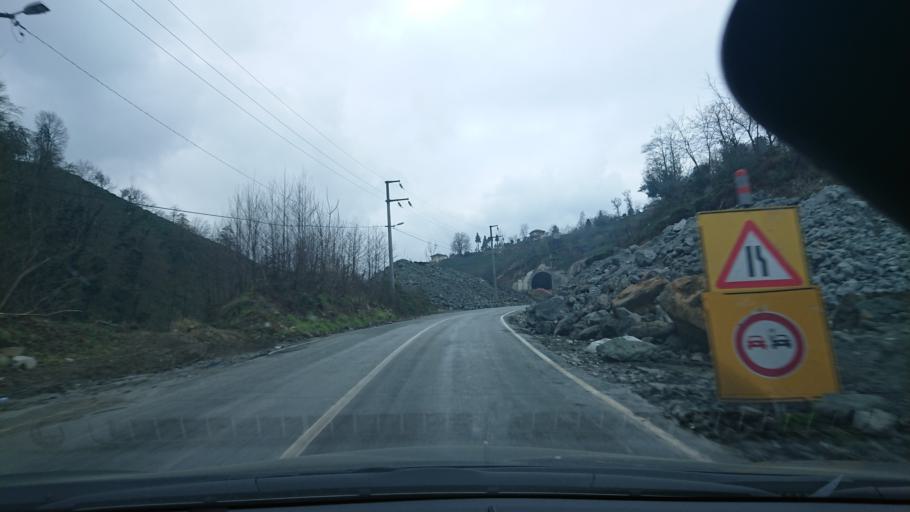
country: TR
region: Rize
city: Rize
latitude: 41.0203
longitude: 40.5019
